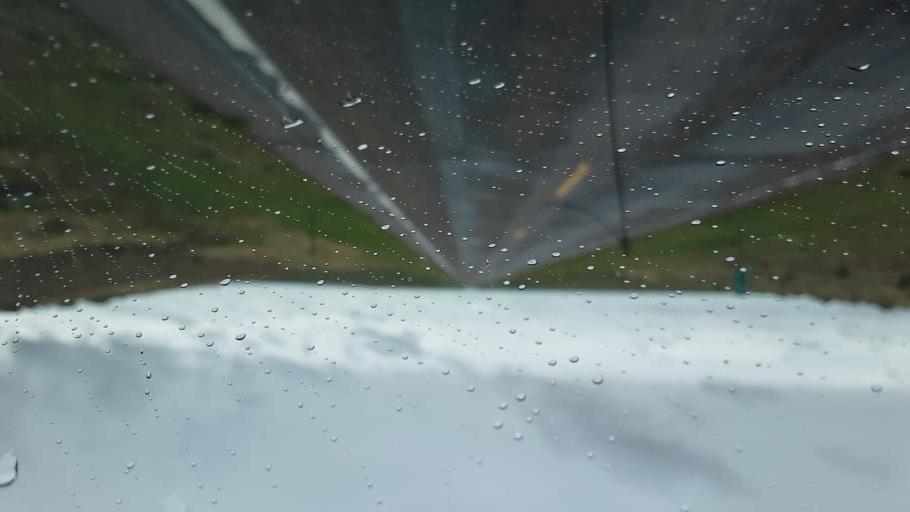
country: US
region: Colorado
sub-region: Lincoln County
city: Hugo
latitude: 38.8495
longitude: -103.2853
